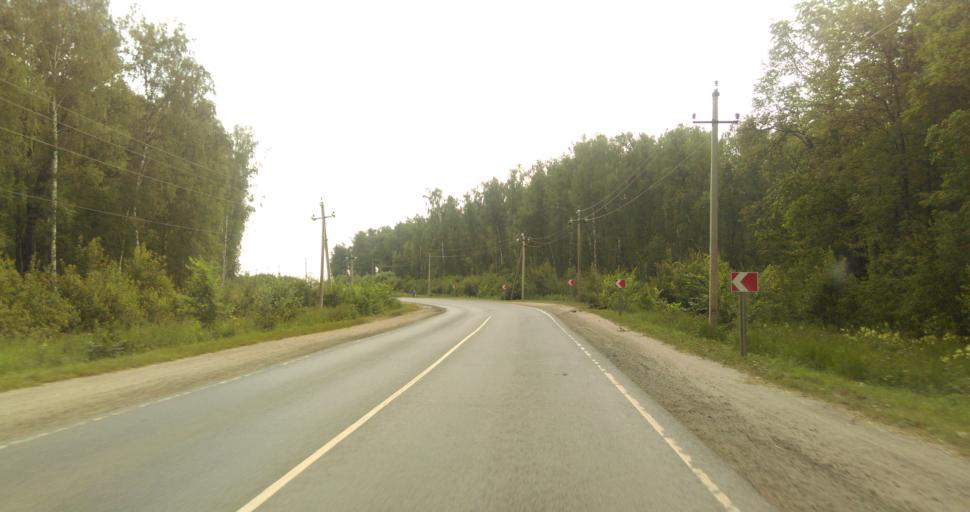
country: RU
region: Moskovskaya
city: Belyye Stolby
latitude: 55.3869
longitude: 37.8635
